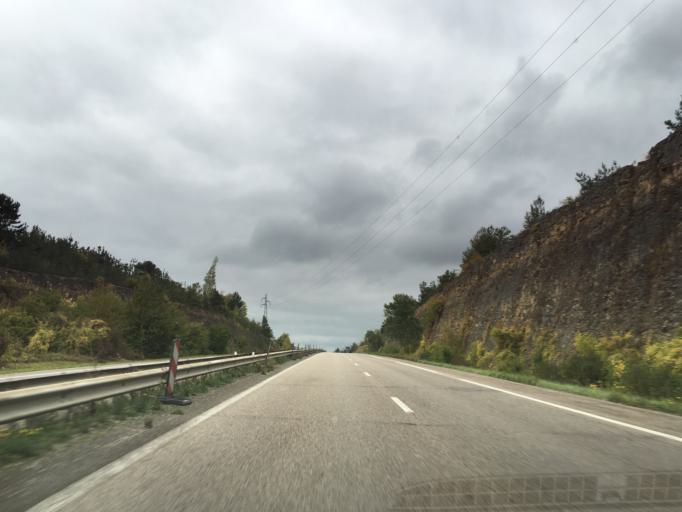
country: FR
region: Lorraine
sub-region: Departement de Meurthe-et-Moselle
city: Foug
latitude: 48.6801
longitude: 5.7492
